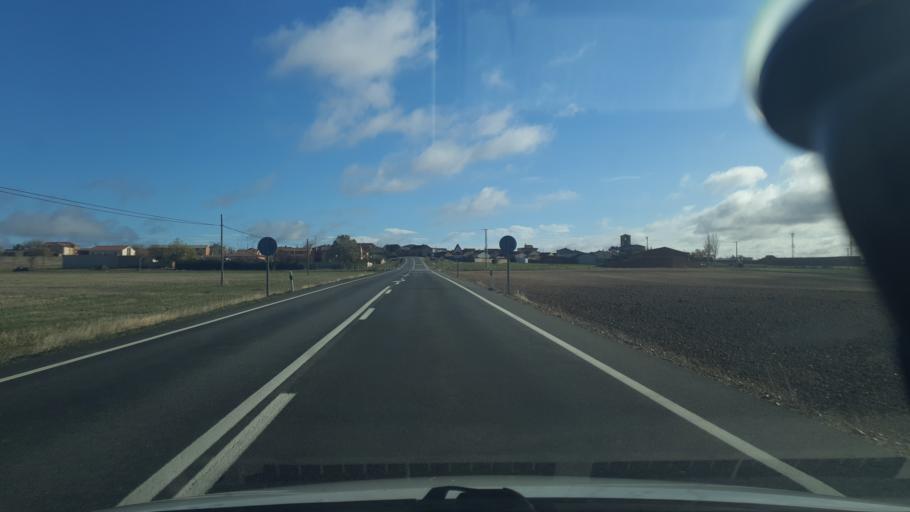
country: ES
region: Castille and Leon
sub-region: Provincia de Segovia
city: Codorniz
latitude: 41.0472
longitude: -4.6341
